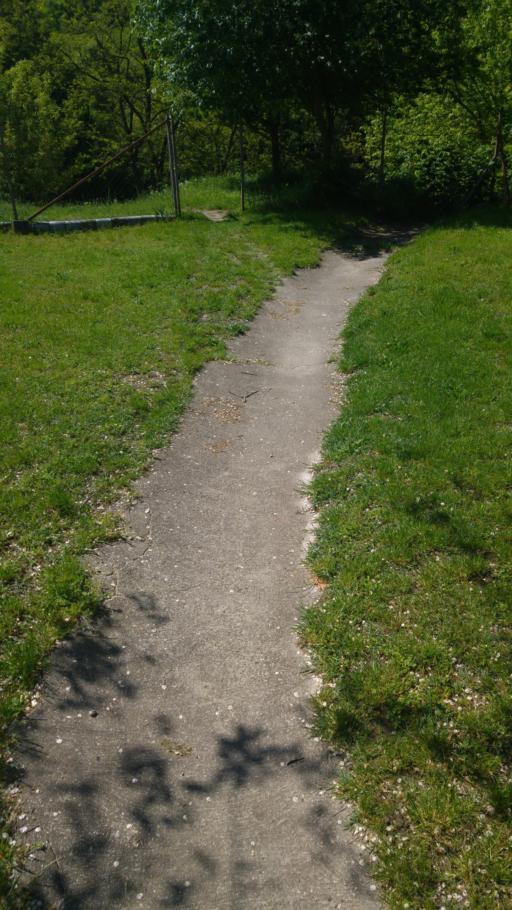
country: HU
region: Komarom-Esztergom
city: Kesztolc
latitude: 47.7116
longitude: 18.7968
